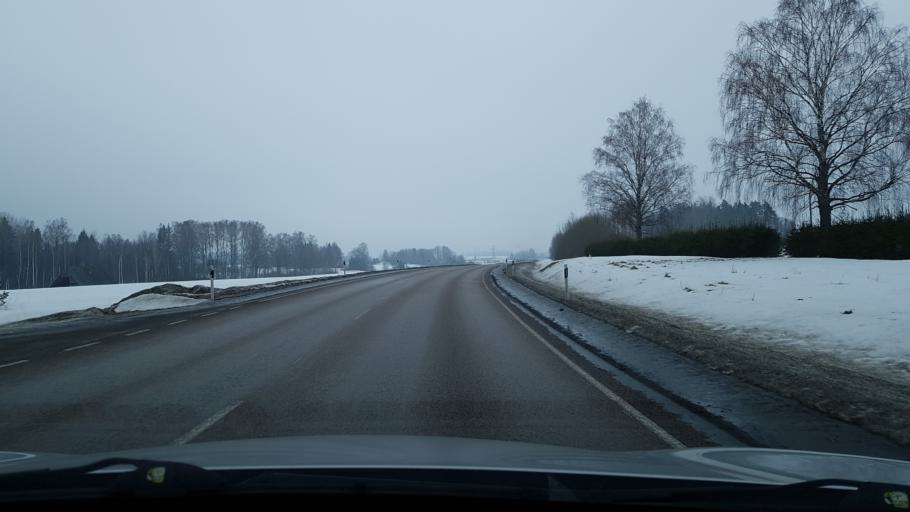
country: EE
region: Valgamaa
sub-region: Torva linn
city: Torva
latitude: 58.0185
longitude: 26.1628
